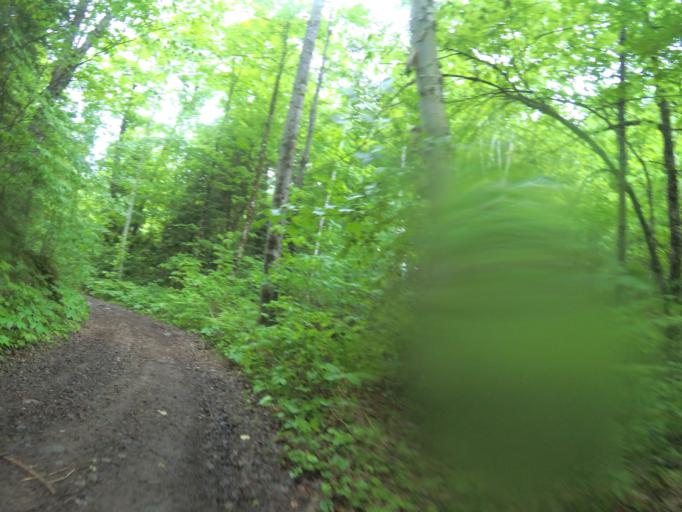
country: CA
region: Ontario
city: Renfrew
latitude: 45.1330
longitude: -76.8211
